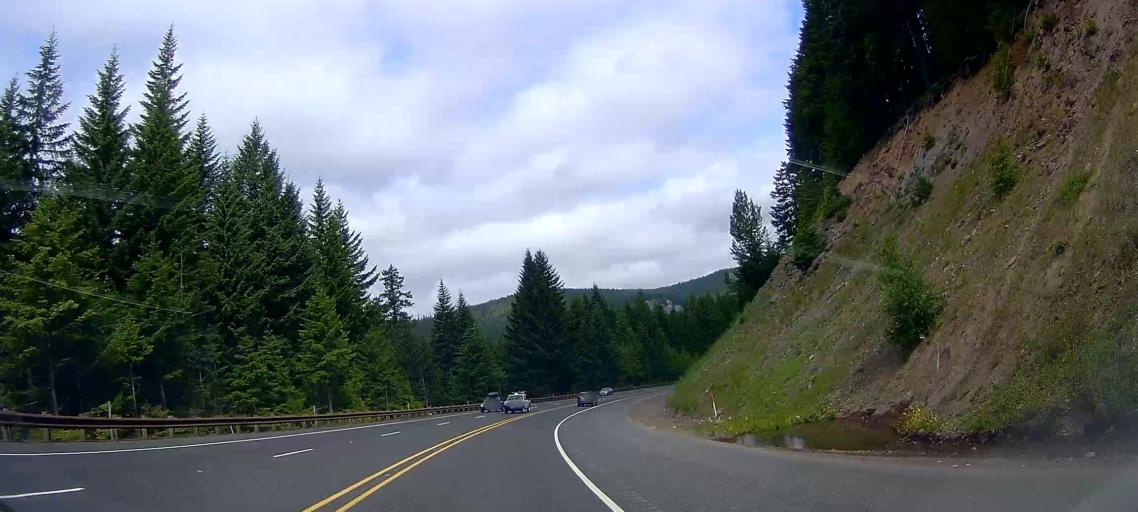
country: US
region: Oregon
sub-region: Clackamas County
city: Mount Hood Village
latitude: 45.2417
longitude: -121.7055
